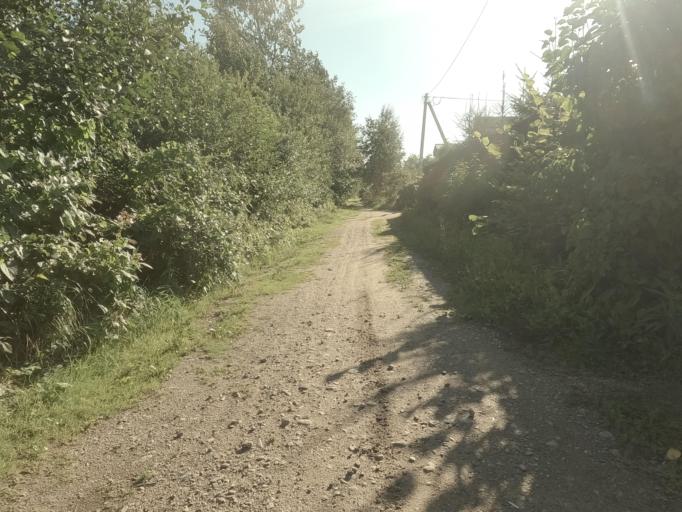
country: RU
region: Leningrad
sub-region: Volosovskiy Rayon
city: Shlissel'burg
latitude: 59.9484
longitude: 31.0120
